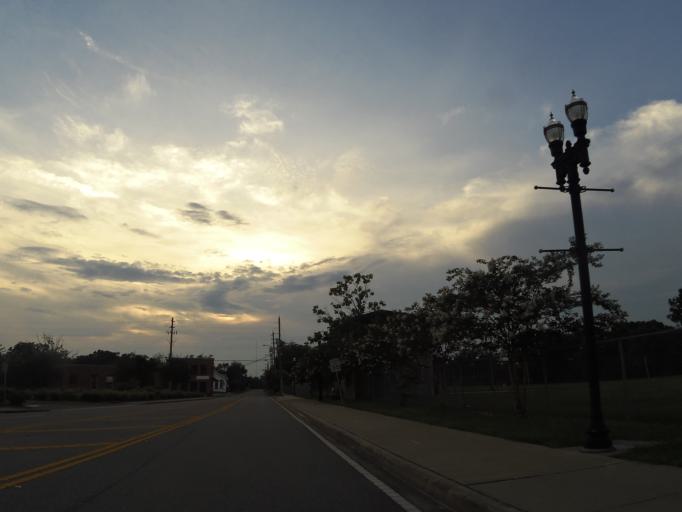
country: US
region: Florida
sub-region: Duval County
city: Jacksonville
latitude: 30.3243
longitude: -81.6827
